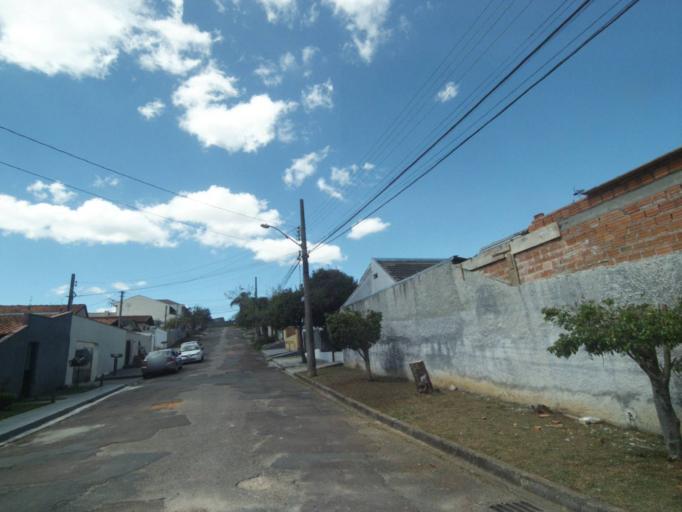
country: BR
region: Parana
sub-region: Curitiba
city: Curitiba
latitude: -25.3800
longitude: -49.2480
